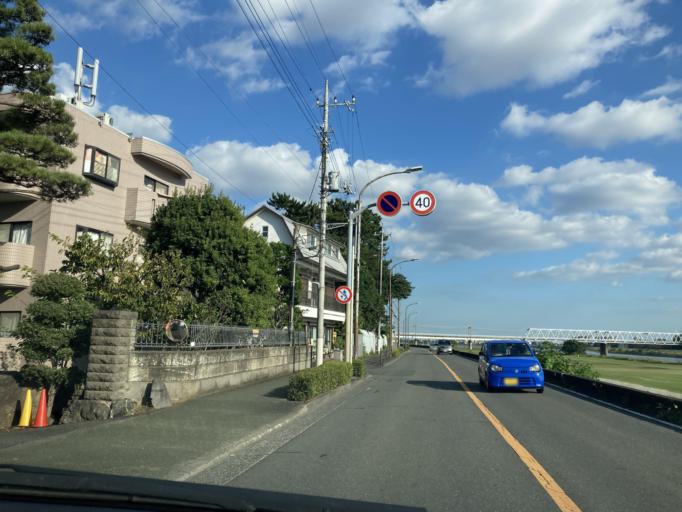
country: JP
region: Tokyo
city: Chofugaoka
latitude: 35.6429
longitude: 139.5307
